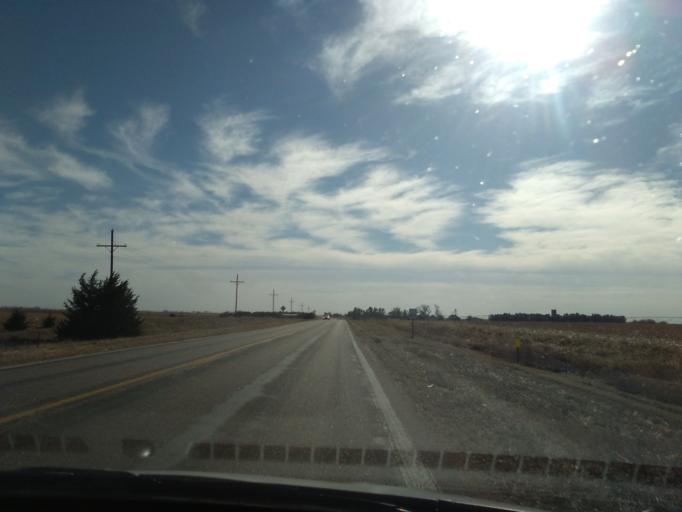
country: US
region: Nebraska
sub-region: Clay County
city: Harvard
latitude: 40.6104
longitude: -98.1089
